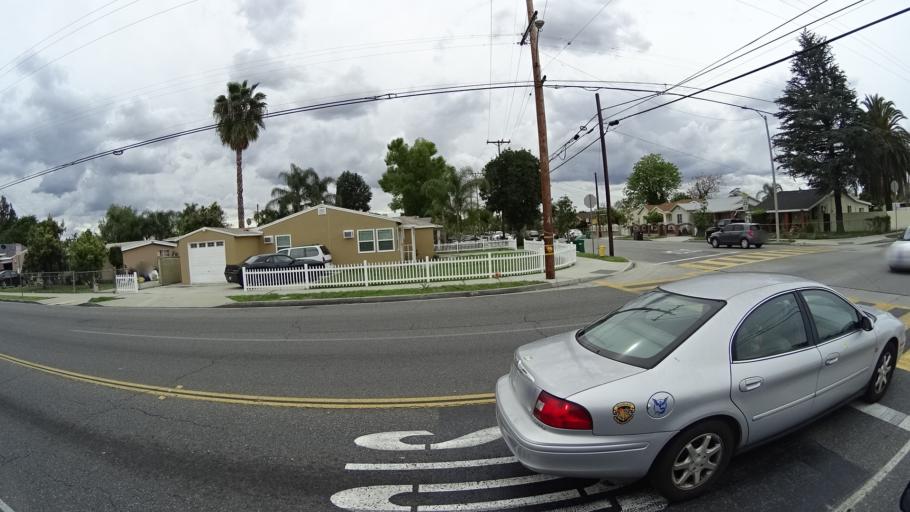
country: US
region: California
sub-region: Los Angeles County
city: Baldwin Park
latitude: 34.0780
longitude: -117.9686
